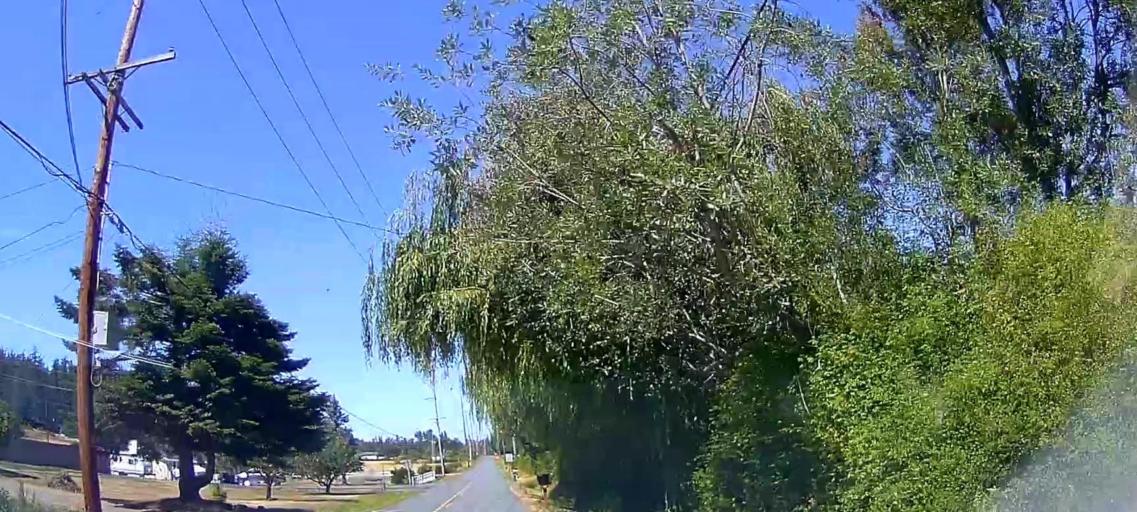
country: US
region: Washington
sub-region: Skagit County
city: Anacortes
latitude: 48.4521
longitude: -122.5656
